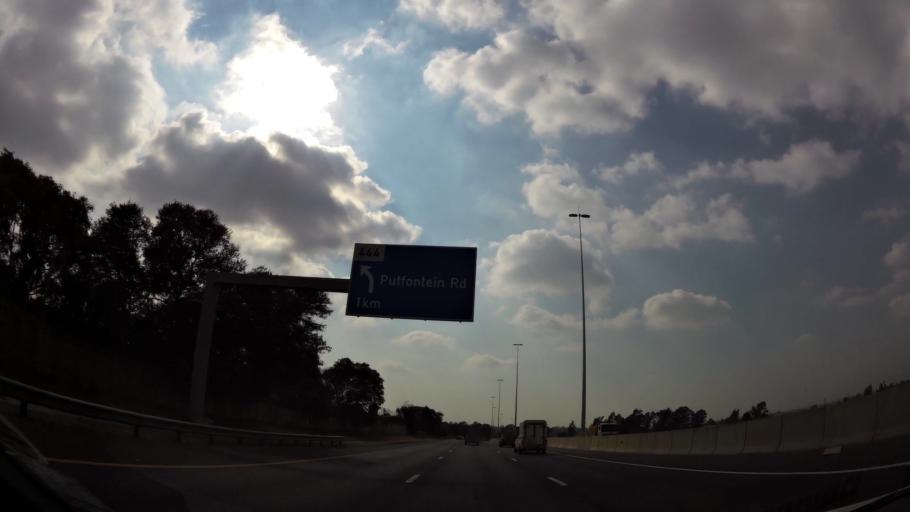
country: ZA
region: Gauteng
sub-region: Ekurhuleni Metropolitan Municipality
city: Benoni
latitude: -26.1657
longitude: 28.3565
